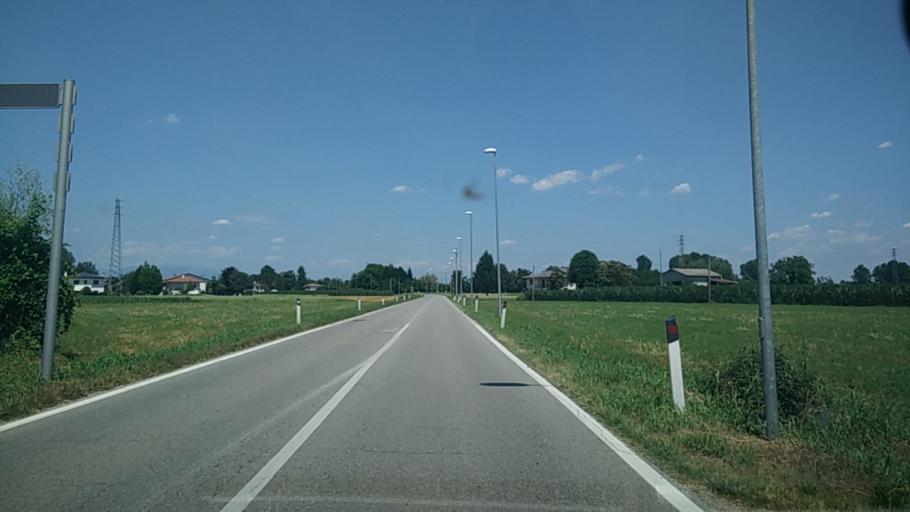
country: IT
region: Veneto
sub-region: Provincia di Padova
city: Tombolo
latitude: 45.6318
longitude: 11.8217
